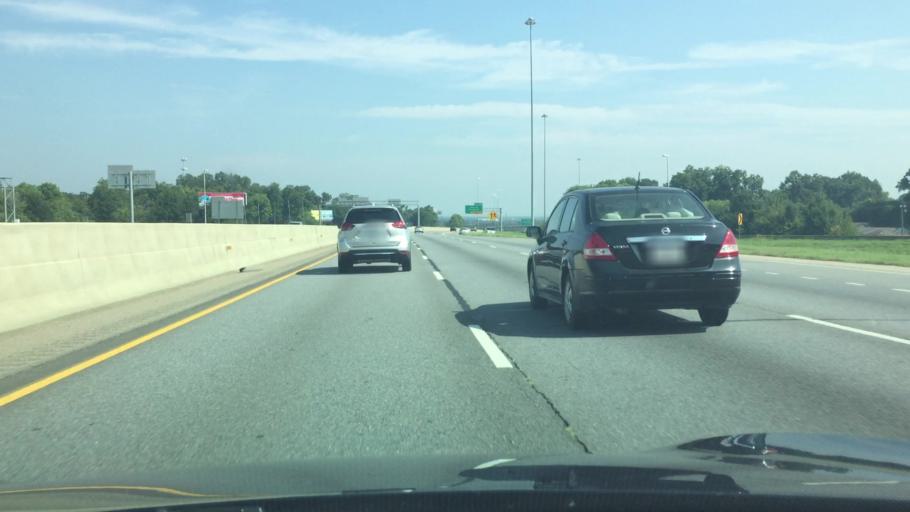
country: US
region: Alabama
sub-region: Montgomery County
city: Montgomery
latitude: 32.3675
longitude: -86.3222
